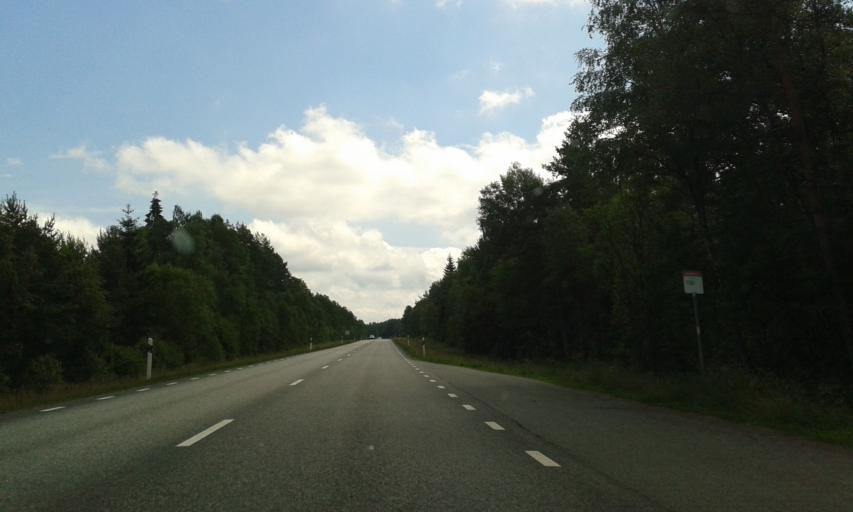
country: SE
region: Joenkoeping
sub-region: Varnamo Kommun
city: Forsheda
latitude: 57.1681
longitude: 13.7779
